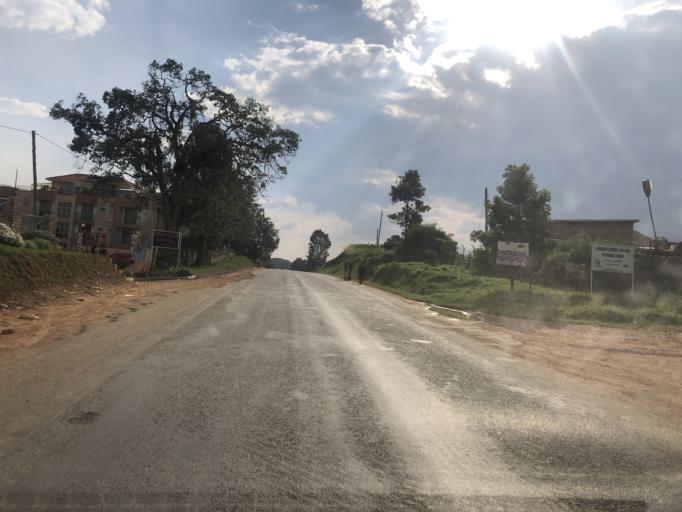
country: UG
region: Western Region
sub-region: Bushenyi District
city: Bushenyi
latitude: -0.5416
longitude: 30.1962
